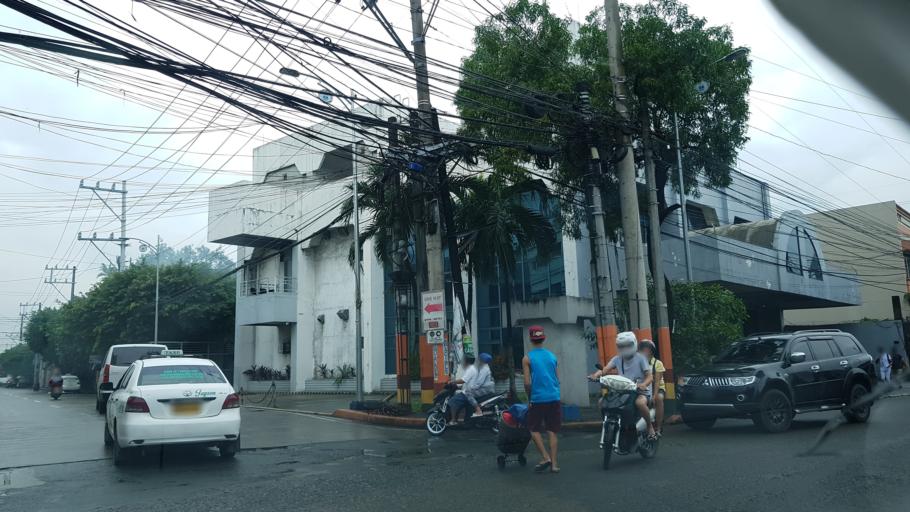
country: PH
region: Metro Manila
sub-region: City of Manila
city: Quiapo
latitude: 14.5800
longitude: 120.9898
